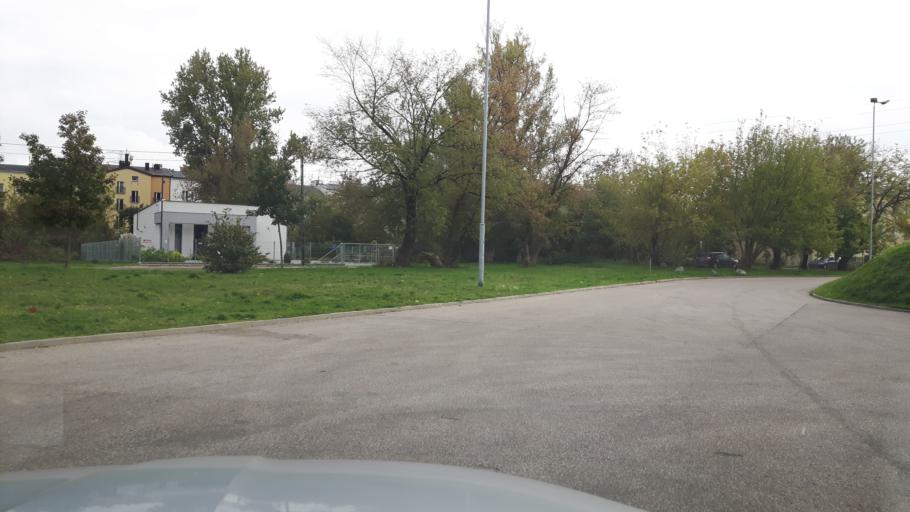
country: PL
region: Masovian Voivodeship
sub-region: Warszawa
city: Praga Polnoc
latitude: 52.2640
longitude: 21.0608
